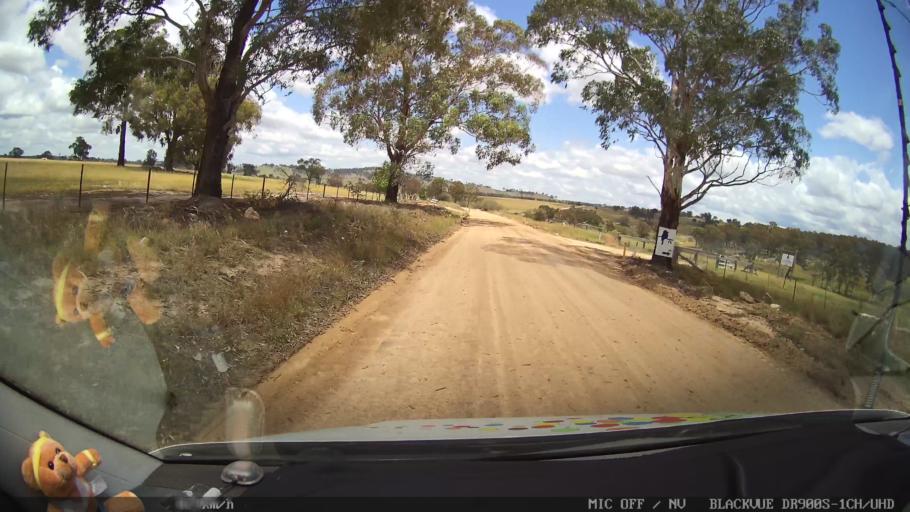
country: AU
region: New South Wales
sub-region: Glen Innes Severn
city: Glen Innes
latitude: -29.3497
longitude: 151.8840
